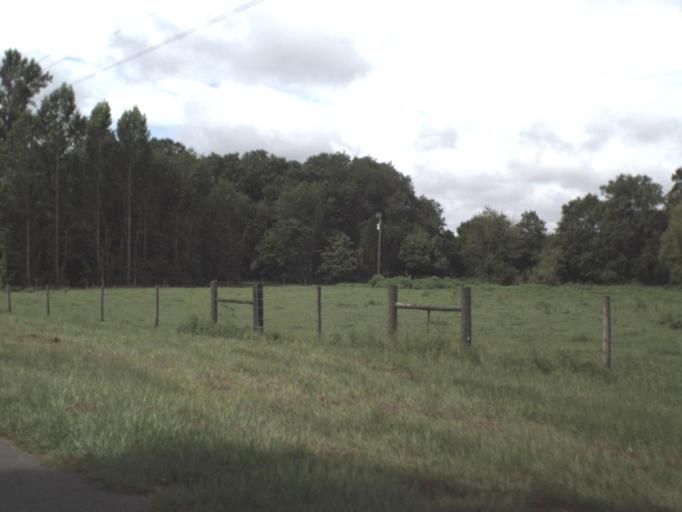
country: US
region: Florida
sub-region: Columbia County
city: Five Points
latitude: 30.3073
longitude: -82.6308
